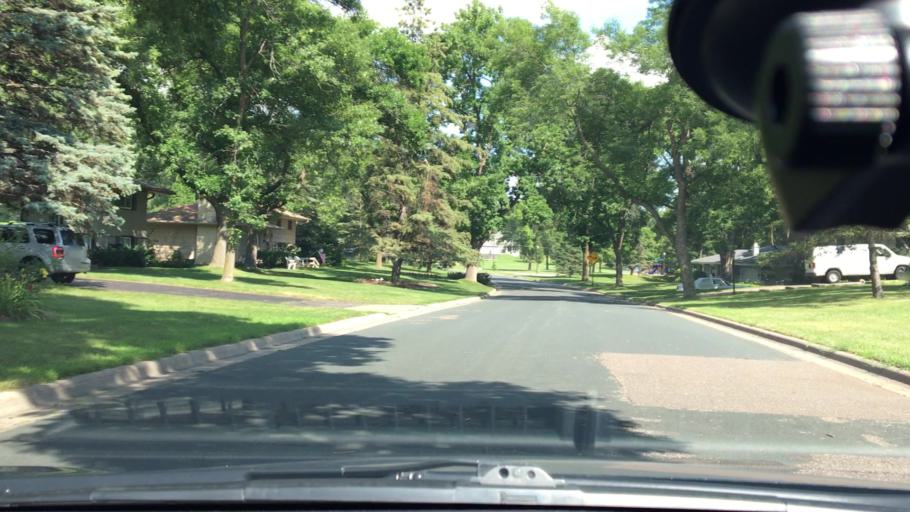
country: US
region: Minnesota
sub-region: Hennepin County
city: Golden Valley
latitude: 44.9974
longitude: -93.3874
